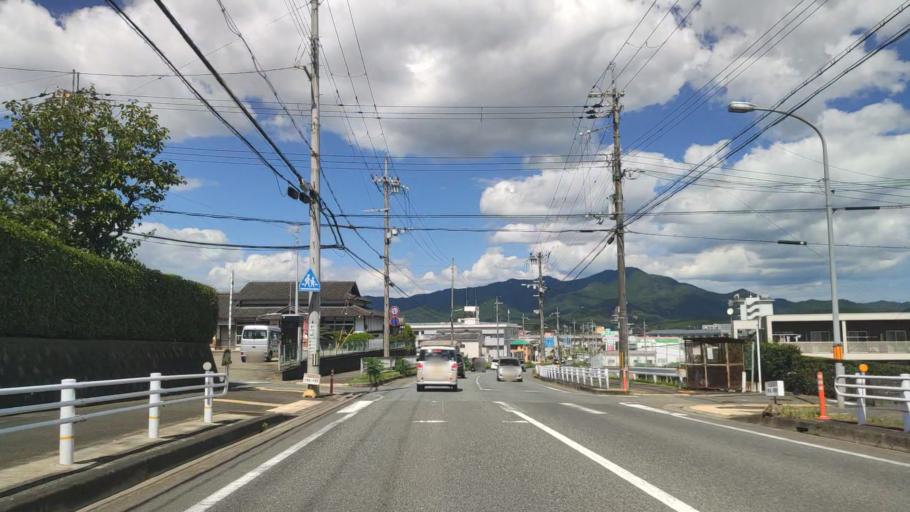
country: JP
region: Kyoto
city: Fukuchiyama
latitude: 35.2862
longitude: 135.1376
